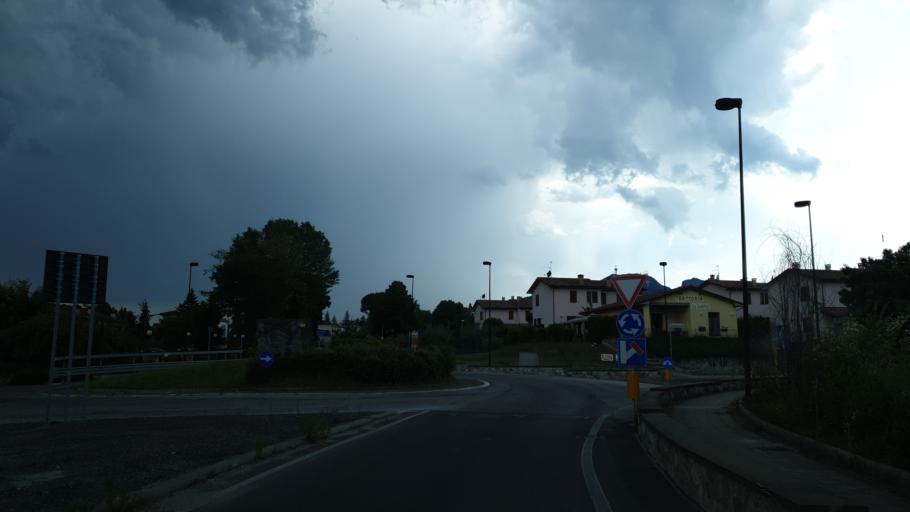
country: IT
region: Emilia-Romagna
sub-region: Provincia di Rimini
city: Secchiano
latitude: 43.9289
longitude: 12.3235
